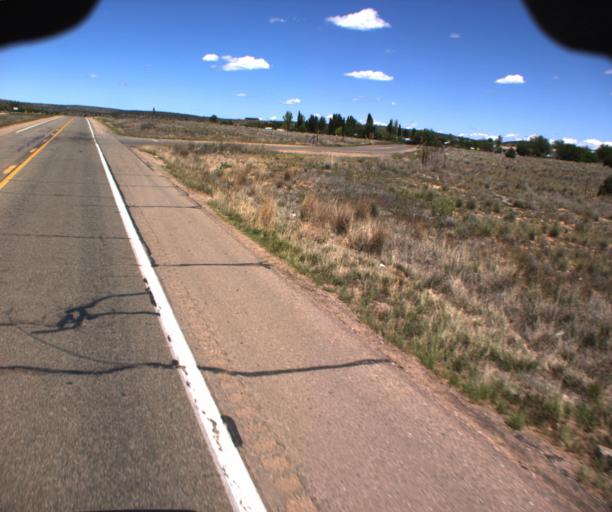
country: US
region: Arizona
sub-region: Yavapai County
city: Paulden
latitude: 34.9038
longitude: -112.4634
